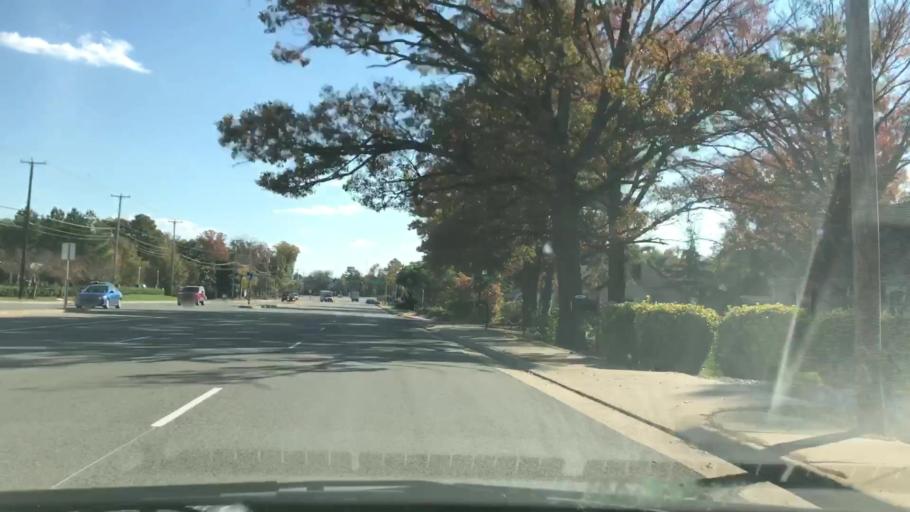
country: US
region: Virginia
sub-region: Henrico County
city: Dumbarton
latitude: 37.6091
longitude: -77.4961
